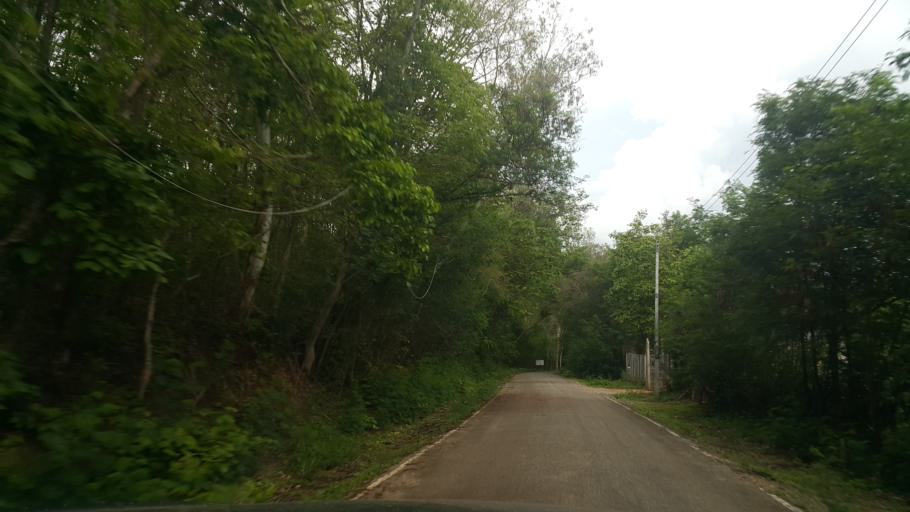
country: TH
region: Chiang Mai
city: Mae On
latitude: 18.7252
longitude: 99.2308
